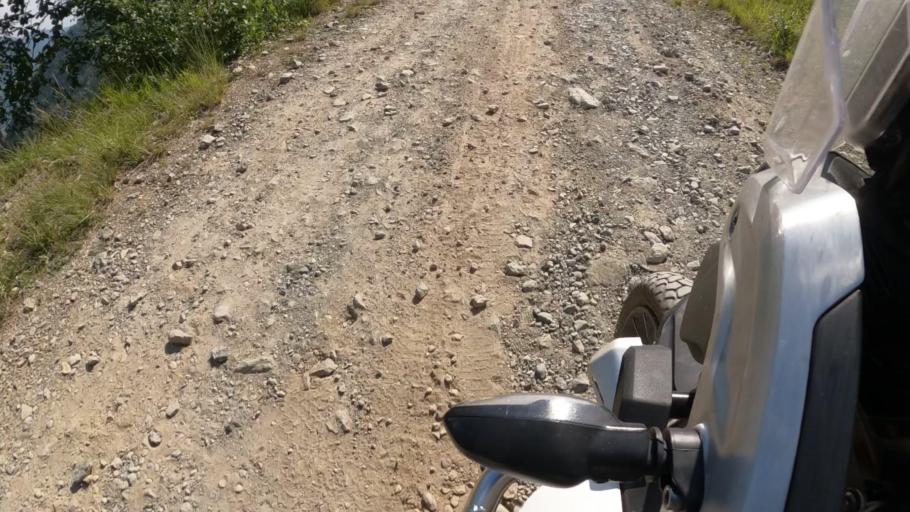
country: IT
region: Piedmont
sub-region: Provincia di Torino
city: Lemie
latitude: 45.2026
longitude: 7.3135
